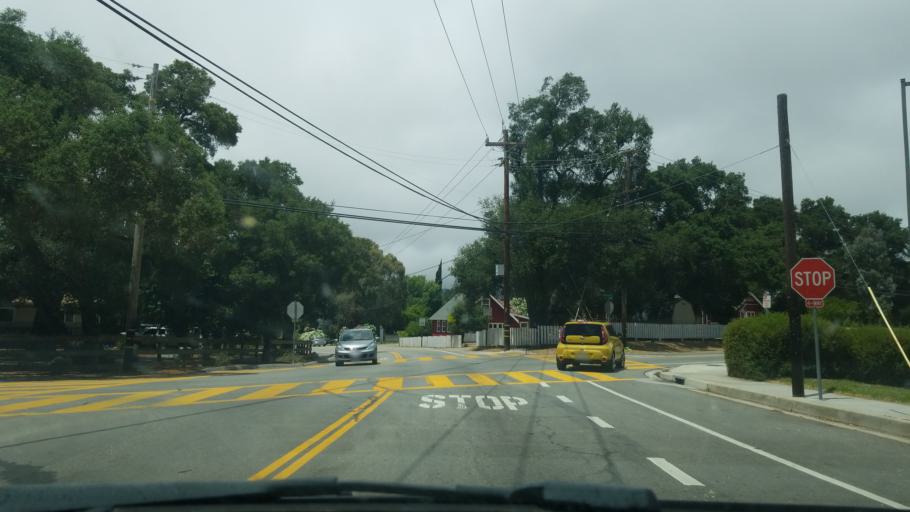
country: US
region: California
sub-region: San Luis Obispo County
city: Atascadero
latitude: 35.4644
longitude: -120.6561
